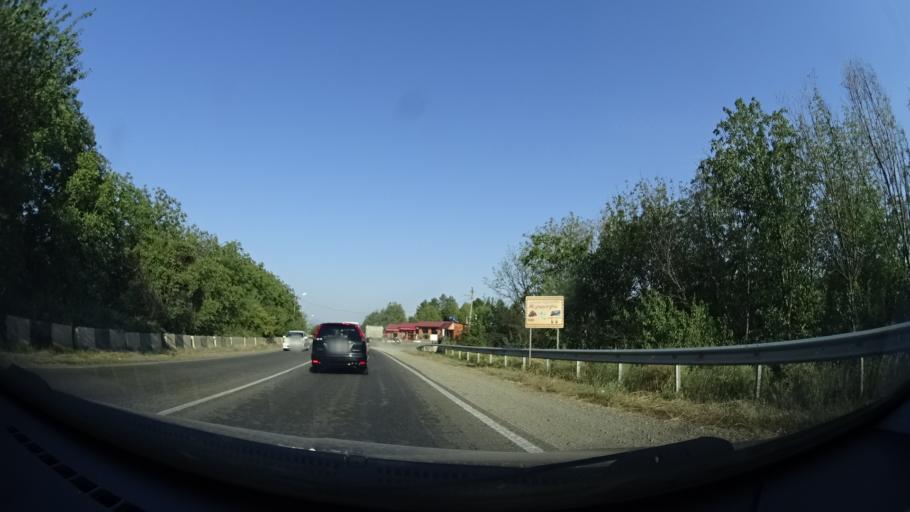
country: GE
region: Kakheti
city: Sagarejo
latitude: 41.6456
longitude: 45.5440
